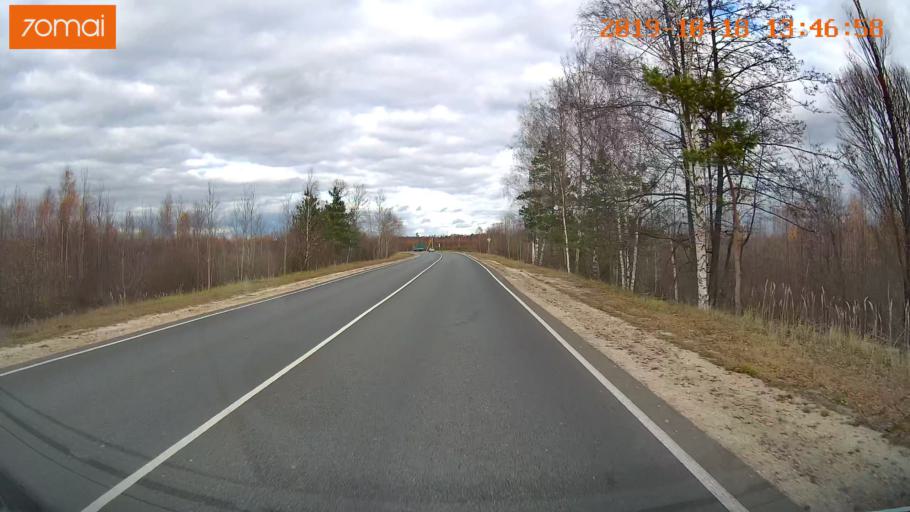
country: RU
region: Rjazan
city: Solotcha
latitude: 54.9678
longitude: 39.9496
